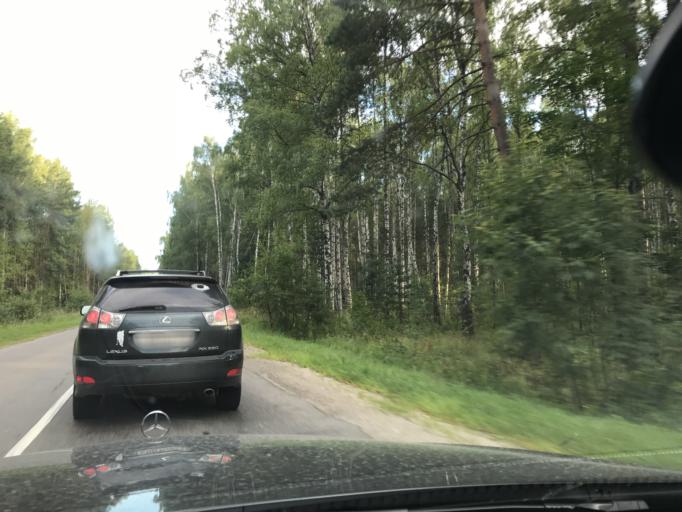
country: RU
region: Vladimir
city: Raduzhnyy
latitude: 55.9988
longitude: 40.2692
